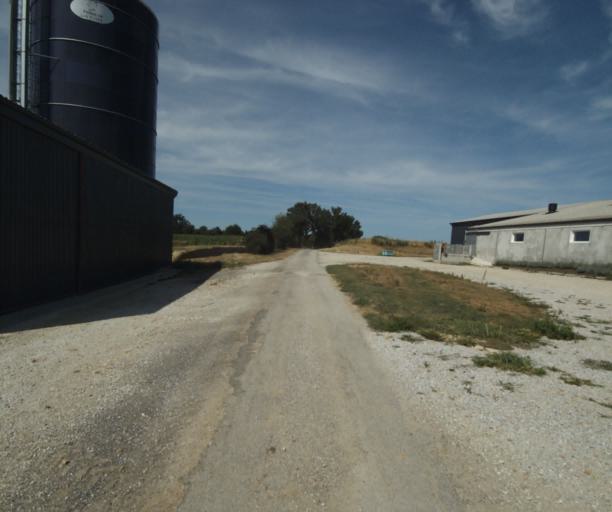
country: FR
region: Midi-Pyrenees
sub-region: Departement du Tarn
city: Soreze
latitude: 43.4980
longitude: 2.0505
